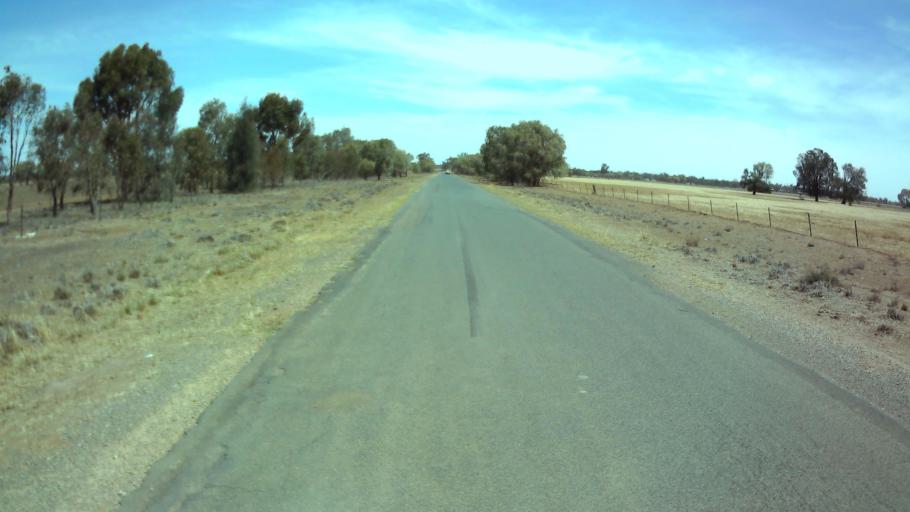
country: AU
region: New South Wales
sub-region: Weddin
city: Grenfell
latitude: -33.8249
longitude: 147.7468
